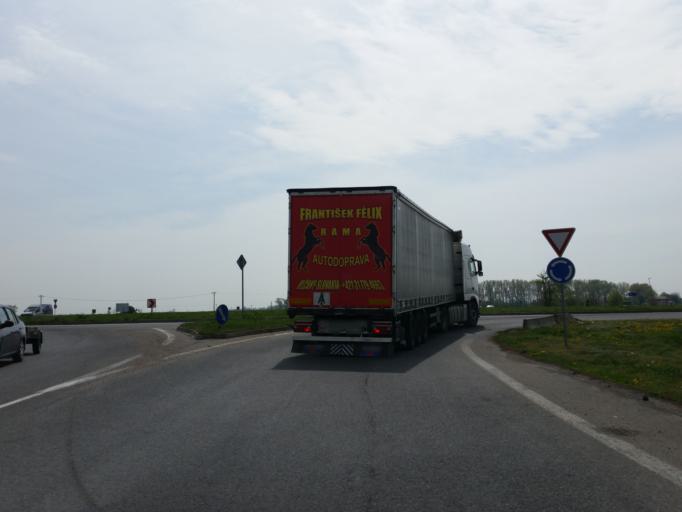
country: SK
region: Trnavsky
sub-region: Okres Galanta
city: Galanta
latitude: 48.2299
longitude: 17.7315
